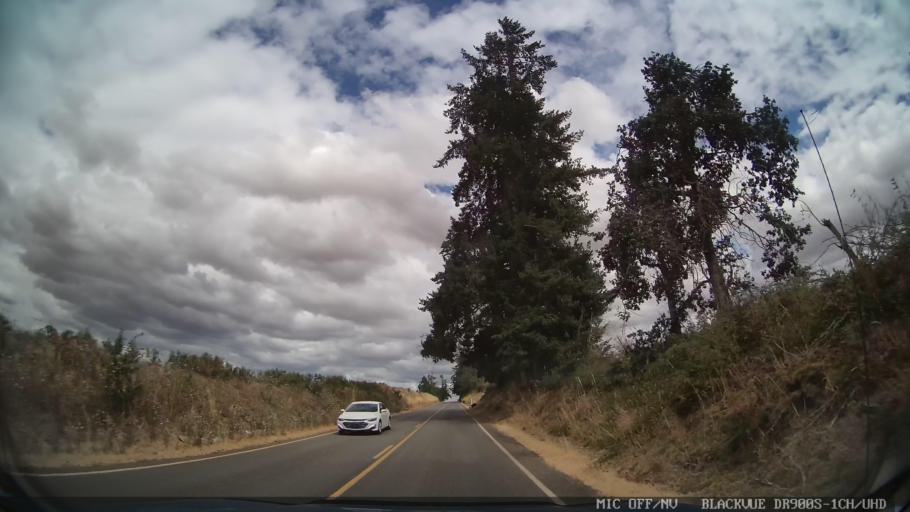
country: US
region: Oregon
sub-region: Marion County
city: Sublimity
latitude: 44.8654
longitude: -122.8195
